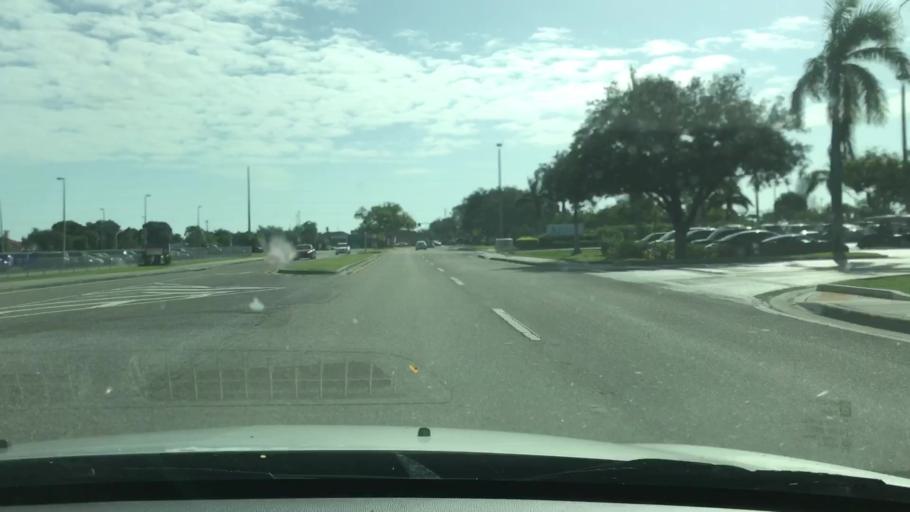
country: US
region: Florida
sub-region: Lee County
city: Lochmoor Waterway Estates
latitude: 26.6412
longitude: -81.9434
